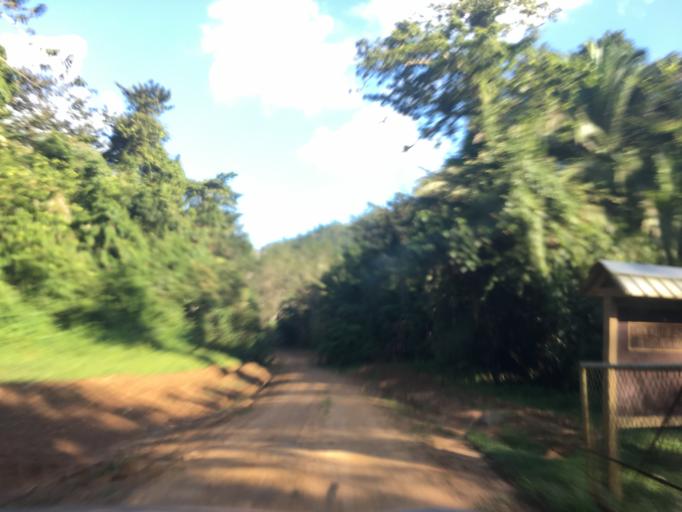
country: BZ
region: Stann Creek
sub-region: Dangriga
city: Dangriga
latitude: 16.7913
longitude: -88.4422
